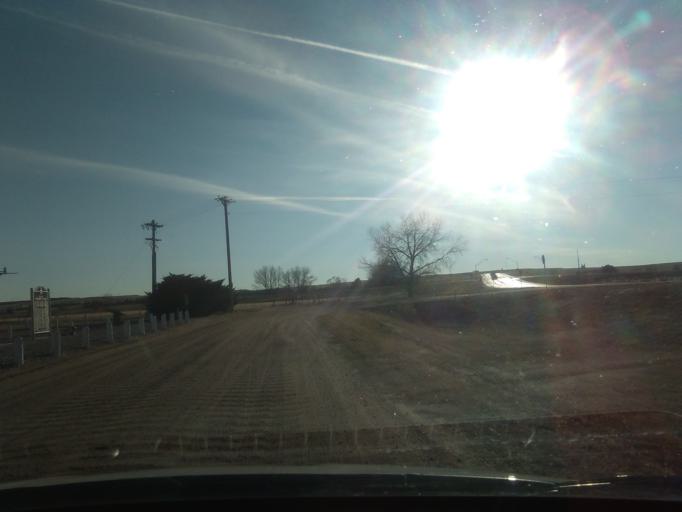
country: US
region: Nebraska
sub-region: Deuel County
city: Chappell
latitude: 41.0841
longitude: -102.4710
